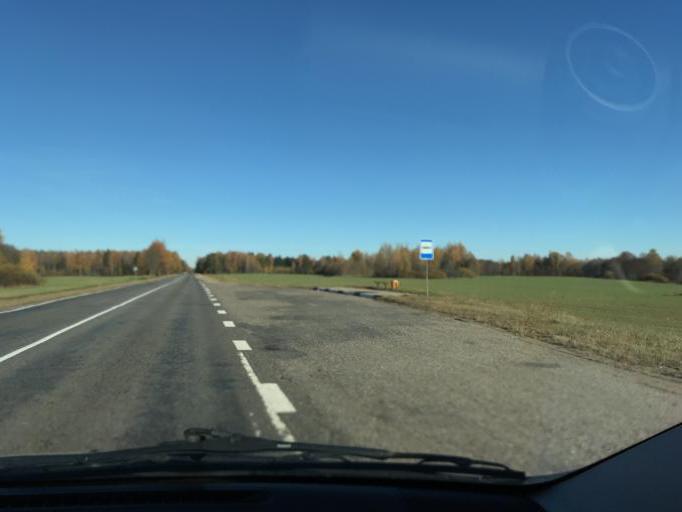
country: BY
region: Vitebsk
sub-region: Ushatski Rayon
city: Ushachy
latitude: 55.0865
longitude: 28.7561
